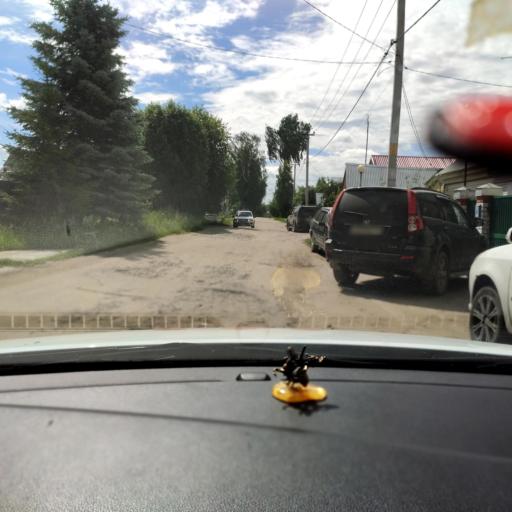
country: RU
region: Tatarstan
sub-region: Zelenodol'skiy Rayon
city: Vasil'yevo
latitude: 55.8385
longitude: 48.7209
